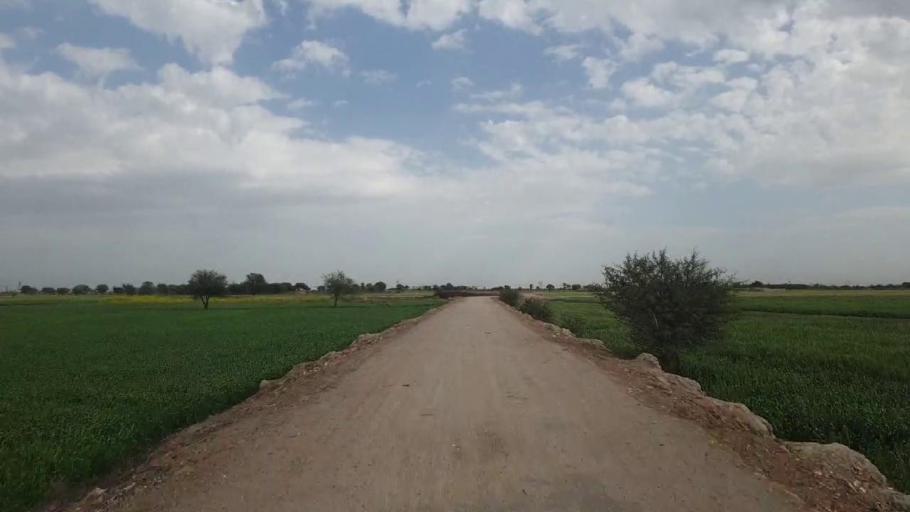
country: PK
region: Sindh
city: Hala
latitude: 25.9310
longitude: 68.4324
